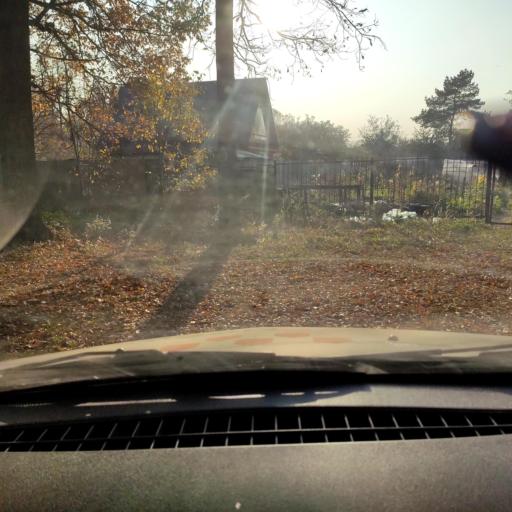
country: RU
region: Bashkortostan
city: Ufa
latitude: 54.8073
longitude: 56.1629
